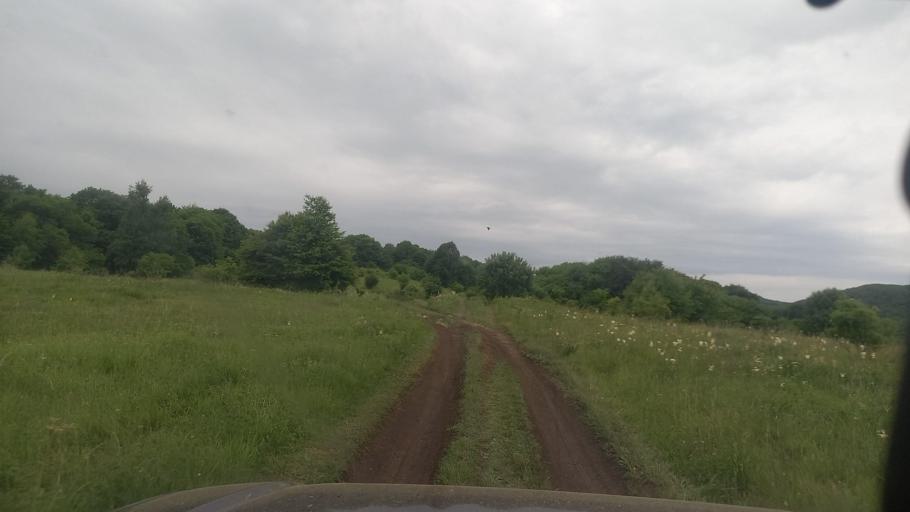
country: RU
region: Karachayevo-Cherkesiya
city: Pregradnaya
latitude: 44.0314
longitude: 41.3087
